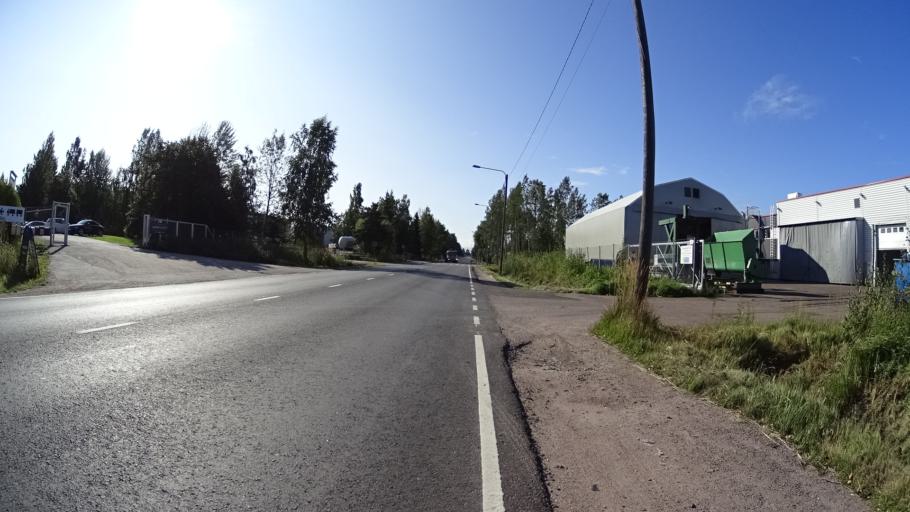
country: FI
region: Uusimaa
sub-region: Helsinki
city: Kilo
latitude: 60.2794
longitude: 24.7617
